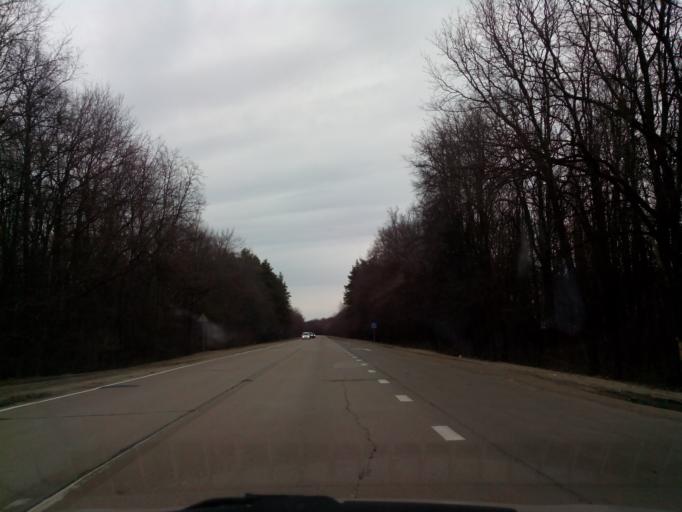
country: RU
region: Tambov
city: Bokino
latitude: 52.5611
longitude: 41.3551
